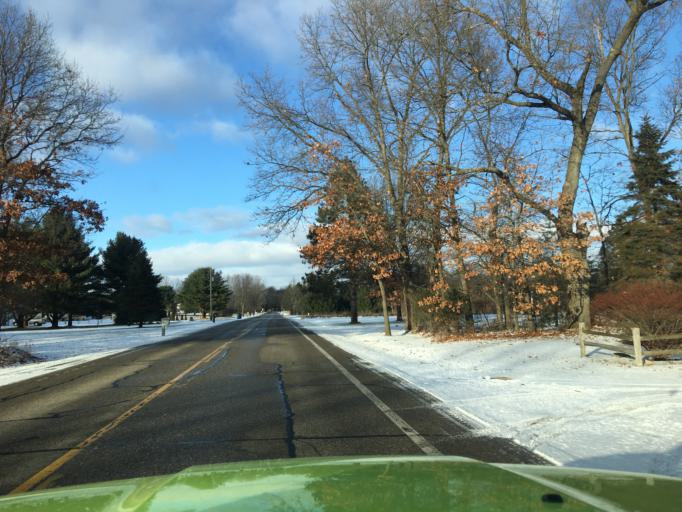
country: US
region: Michigan
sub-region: Montcalm County
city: Greenville
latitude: 43.2023
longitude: -85.2826
